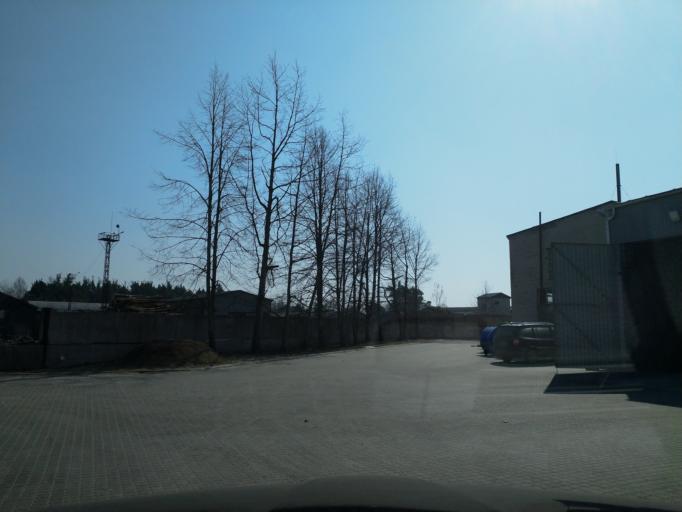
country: LV
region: Kuldigas Rajons
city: Kuldiga
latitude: 56.9676
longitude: 21.9249
